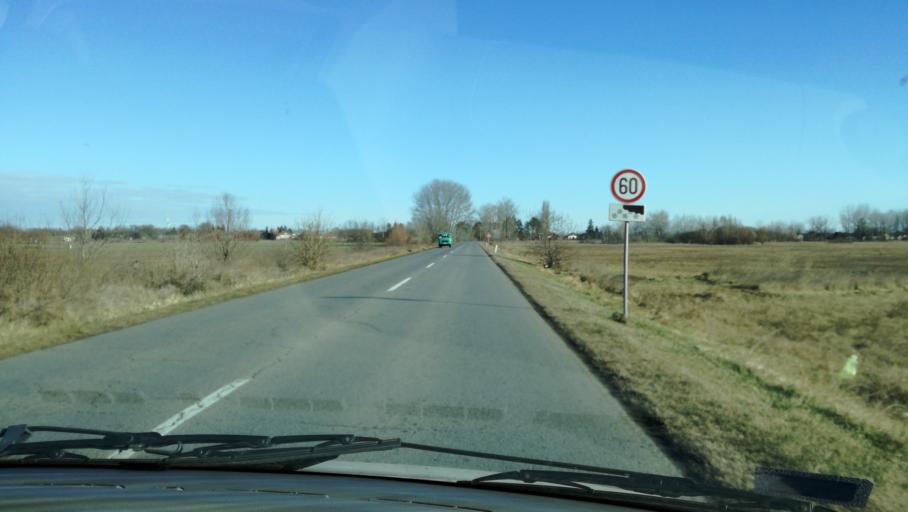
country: HU
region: Csongrad
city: Asotthalom
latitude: 46.1118
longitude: 19.8336
